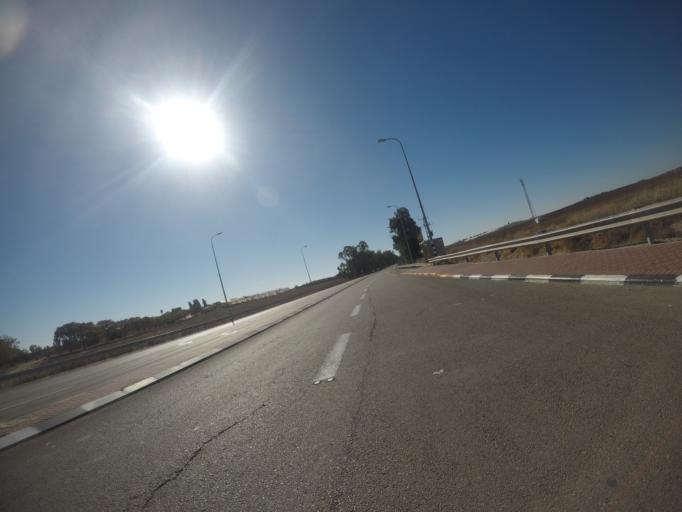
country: IL
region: Southern District
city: Qiryat Gat
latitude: 31.6456
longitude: 34.6995
